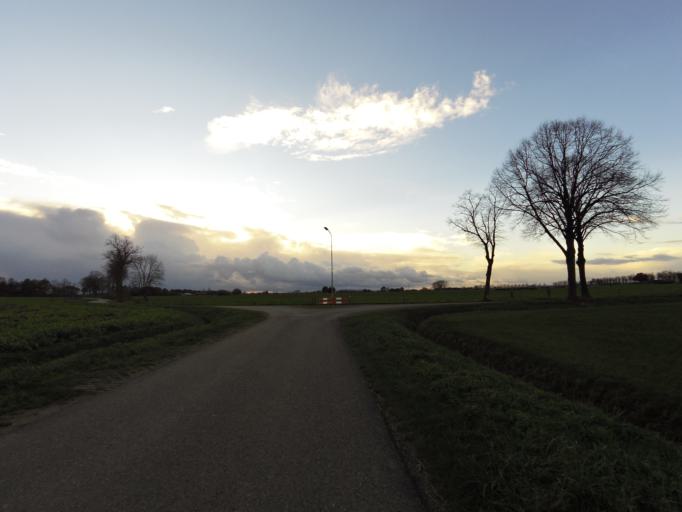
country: NL
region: Gelderland
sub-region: Oude IJsselstreek
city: Gendringen
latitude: 51.8458
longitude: 6.3800
